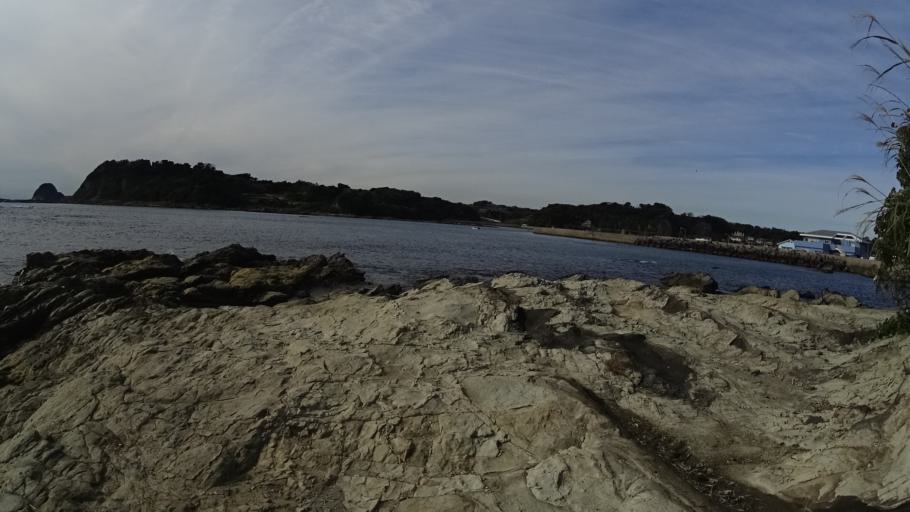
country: JP
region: Kanagawa
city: Miura
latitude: 35.1415
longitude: 139.6691
